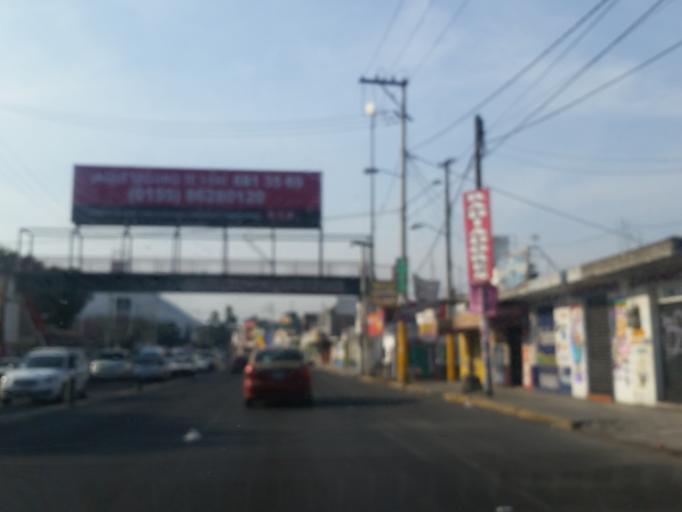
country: MX
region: Mexico
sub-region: La Paz
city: San Isidro
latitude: 19.3279
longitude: -98.9472
